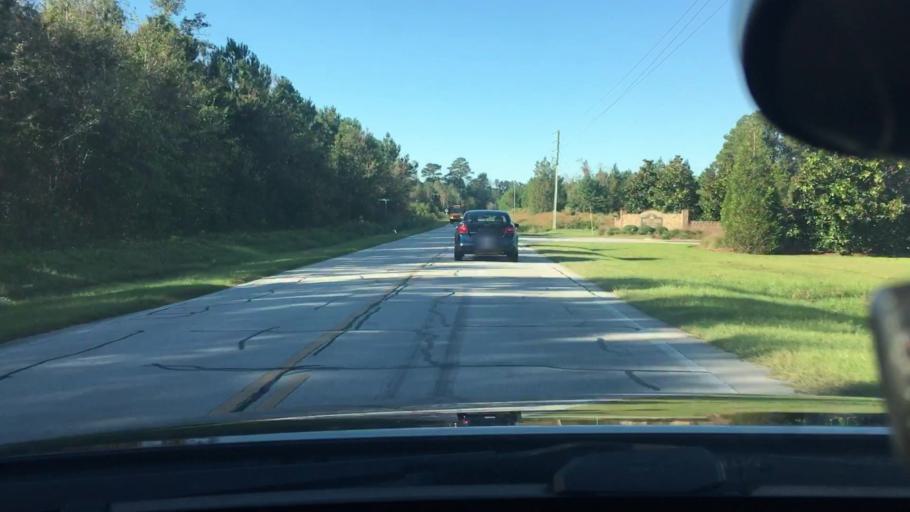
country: US
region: North Carolina
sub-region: Craven County
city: Vanceboro
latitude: 35.2806
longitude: -77.1530
